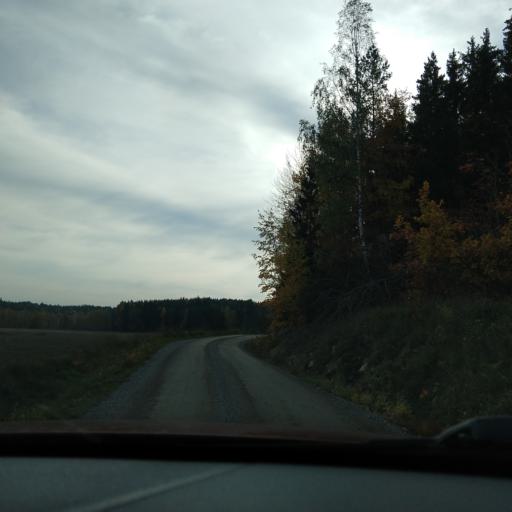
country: SE
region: Stockholm
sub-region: Vallentuna Kommun
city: Vallentuna
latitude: 59.5387
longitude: 18.0185
